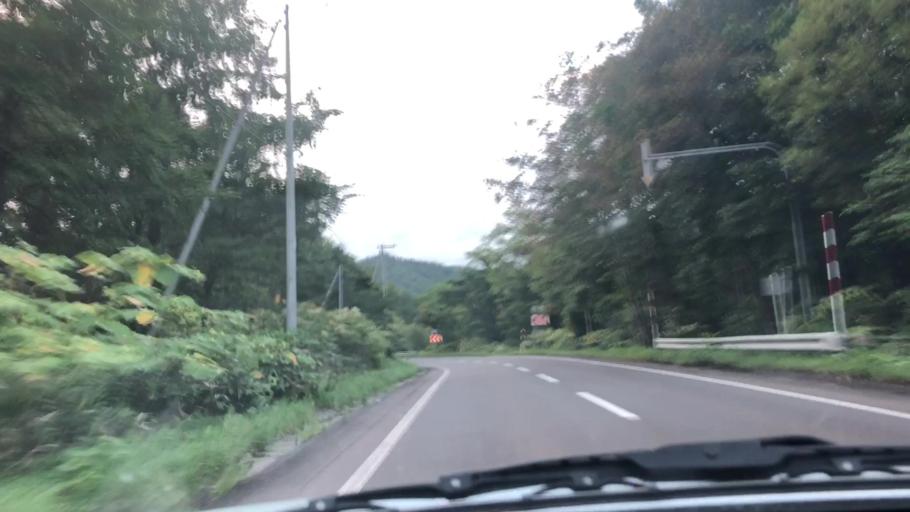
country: JP
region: Hokkaido
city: Chitose
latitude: 42.8773
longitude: 142.1286
